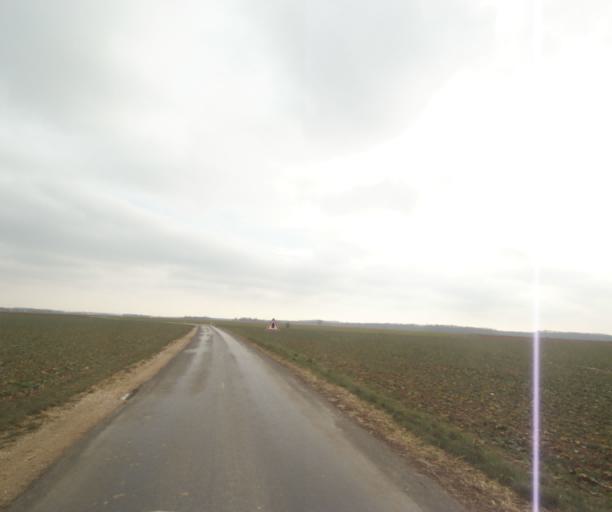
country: FR
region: Champagne-Ardenne
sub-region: Departement de la Haute-Marne
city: Villiers-en-Lieu
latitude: 48.6815
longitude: 4.8437
